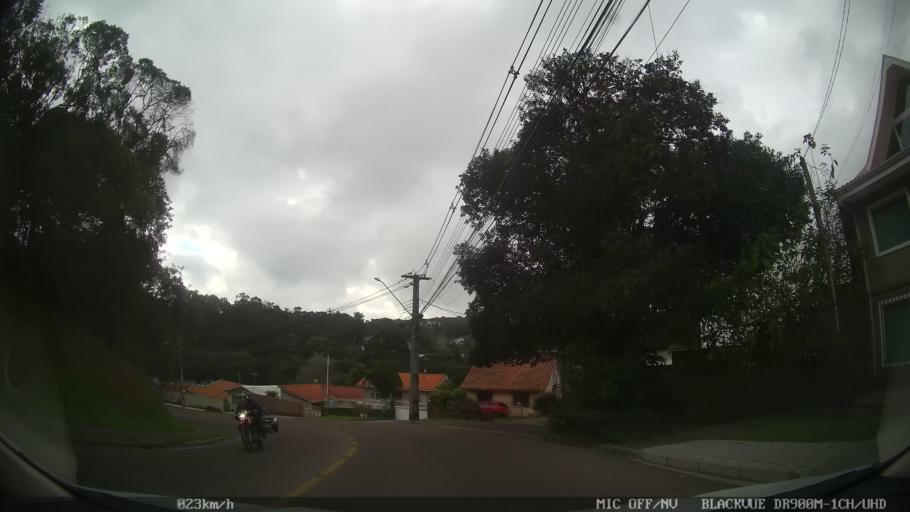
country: BR
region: Parana
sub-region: Curitiba
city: Curitiba
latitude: -25.3644
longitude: -49.2551
